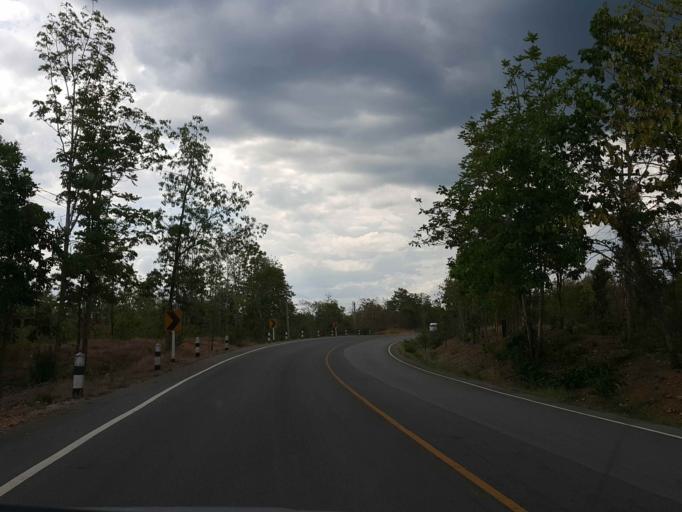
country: TH
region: Sukhothai
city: Thung Saliam
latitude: 17.3535
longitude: 99.4143
